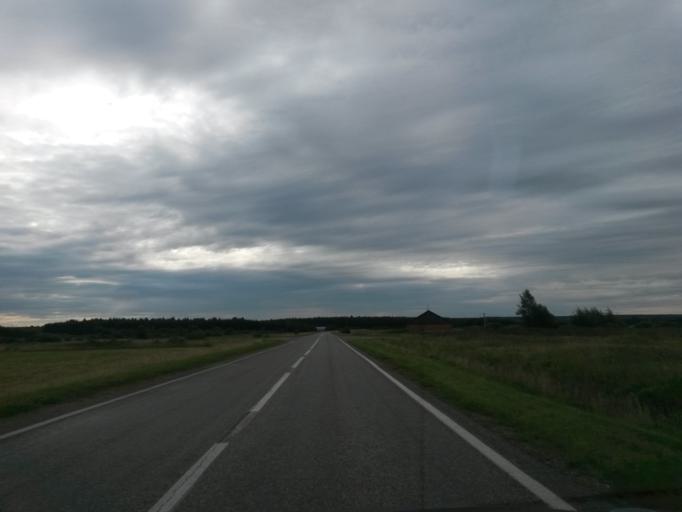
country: RU
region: Jaroslavl
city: Gavrilov-Yam
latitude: 57.3273
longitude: 39.8531
